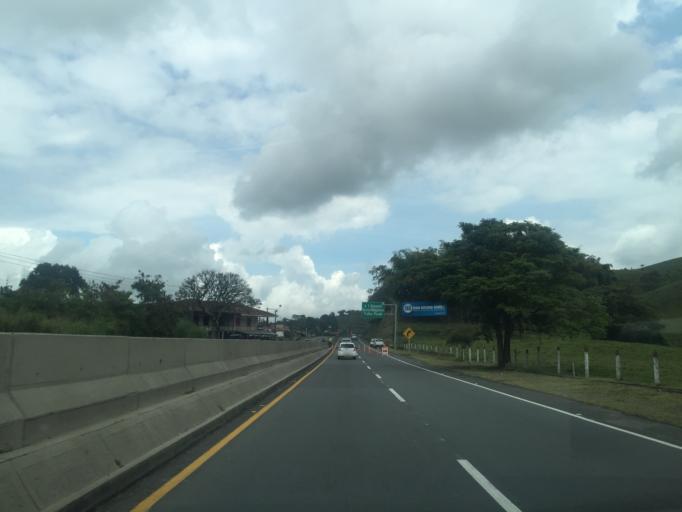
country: CO
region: Risaralda
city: Santa Rosa de Cabal
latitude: 4.9011
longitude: -75.6274
